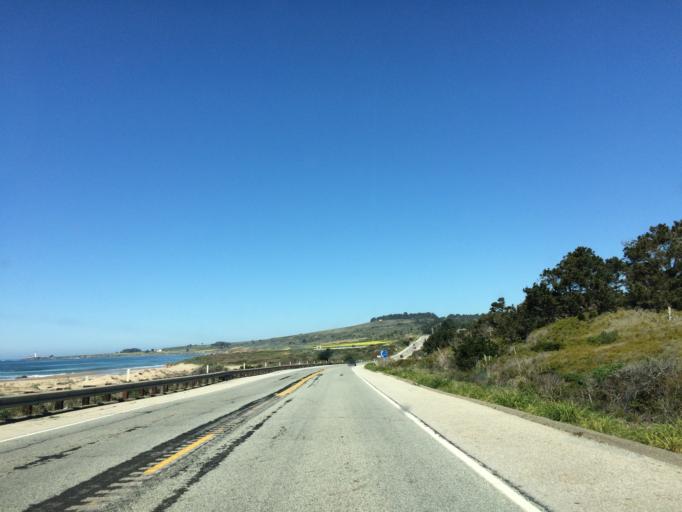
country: US
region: California
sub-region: Santa Cruz County
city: Boulder Creek
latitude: 37.1625
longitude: -122.3589
